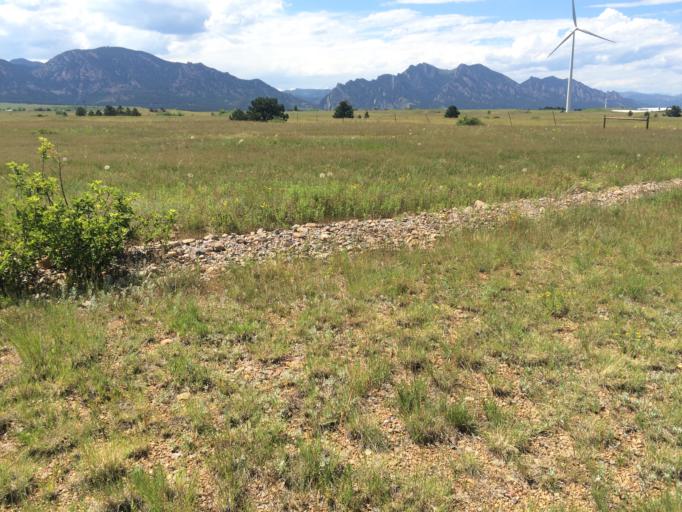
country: US
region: Colorado
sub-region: Boulder County
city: Superior
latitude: 39.8995
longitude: -105.2220
